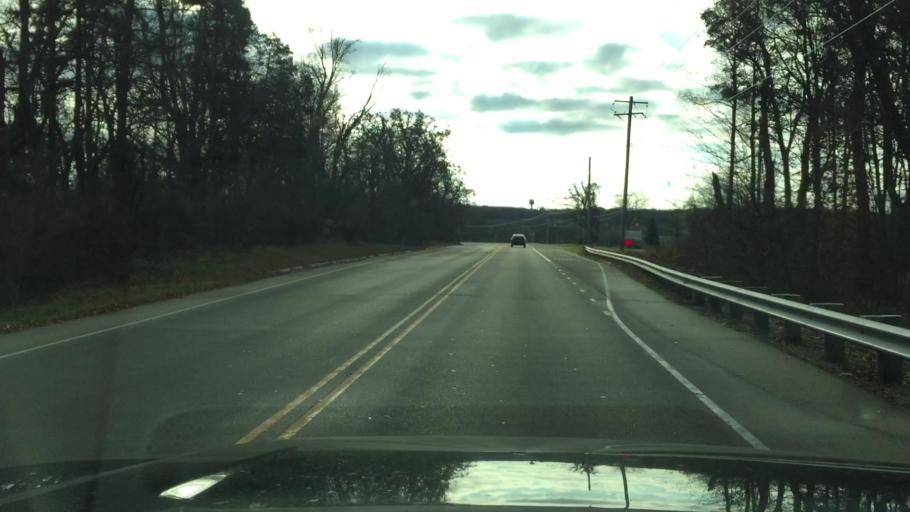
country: US
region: Wisconsin
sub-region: Walworth County
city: Williams Bay
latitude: 42.5886
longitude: -88.5313
